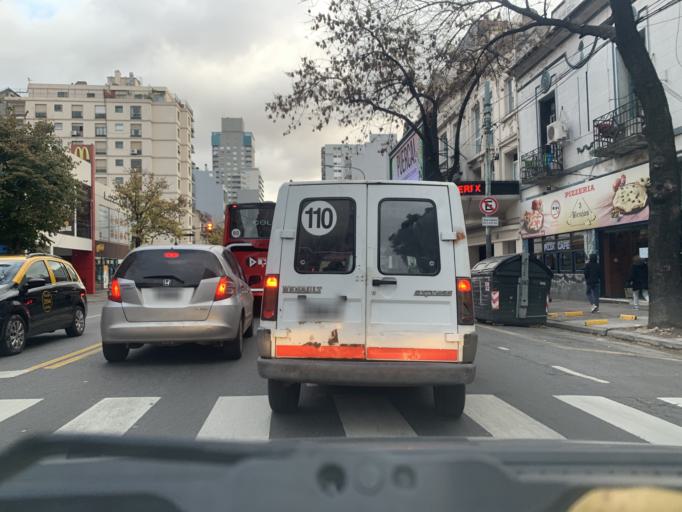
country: AR
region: Buenos Aires F.D.
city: Colegiales
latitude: -34.5799
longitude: -58.4506
